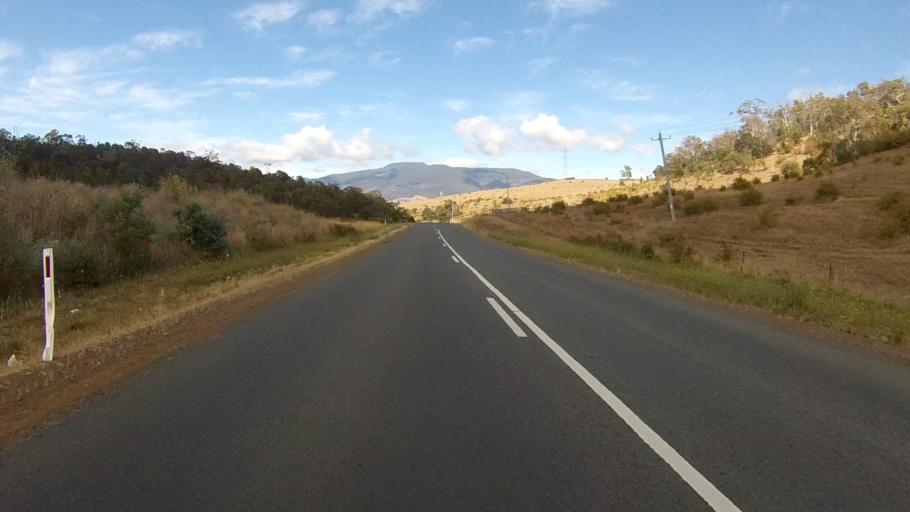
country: AU
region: Tasmania
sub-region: Brighton
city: Old Beach
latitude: -42.7414
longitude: 147.2873
